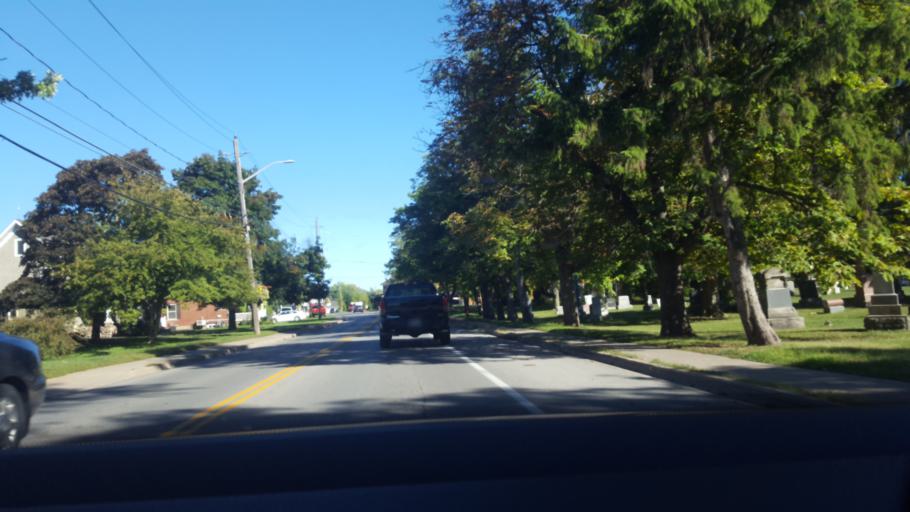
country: CA
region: Ontario
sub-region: Regional Municipality of Niagara
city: St. Catharines
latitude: 43.1003
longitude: -79.5489
